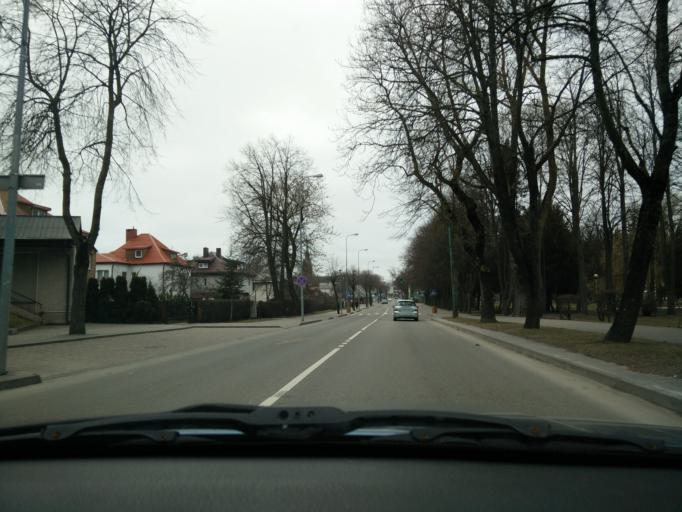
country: LT
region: Klaipedos apskritis
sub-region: Klaipeda
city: Palanga
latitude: 55.9163
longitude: 21.0736
